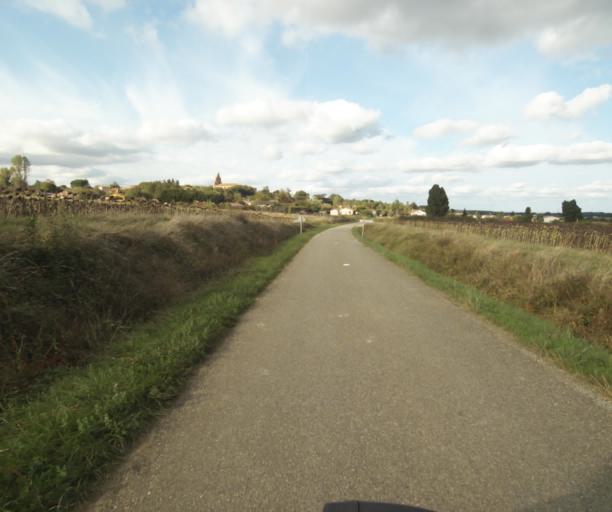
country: FR
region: Midi-Pyrenees
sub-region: Departement de la Haute-Garonne
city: Launac
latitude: 43.8388
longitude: 1.1208
